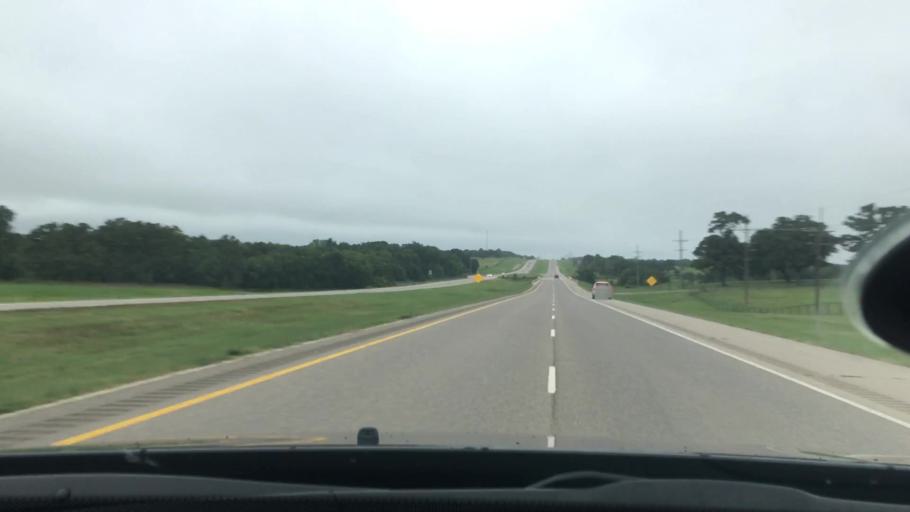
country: US
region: Oklahoma
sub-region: Lincoln County
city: Prague
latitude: 35.3565
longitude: -96.6715
